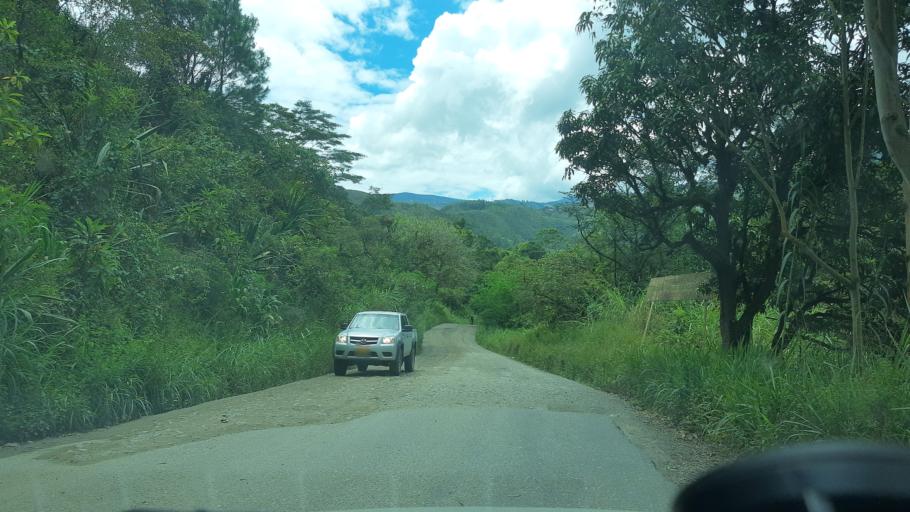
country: CO
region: Cundinamarca
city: Tenza
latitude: 5.0263
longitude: -73.3893
